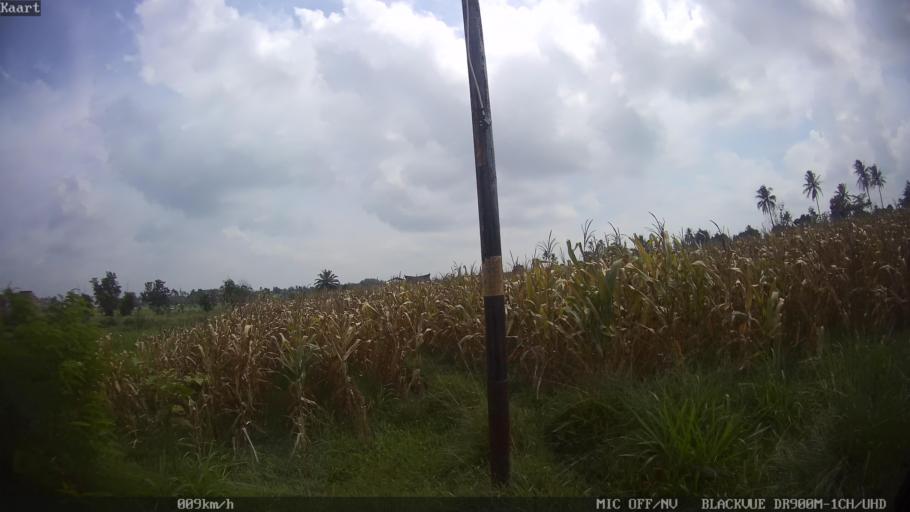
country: ID
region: Lampung
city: Kedaton
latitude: -5.3312
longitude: 105.3001
